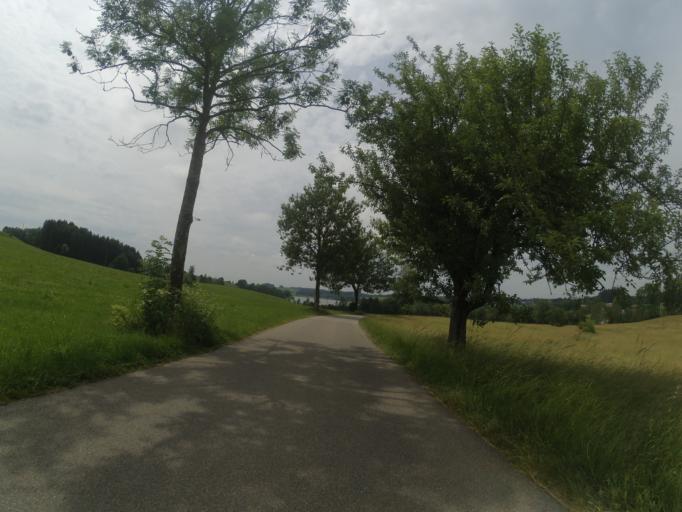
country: DE
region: Baden-Wuerttemberg
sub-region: Tuebingen Region
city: Isny im Allgau
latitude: 47.7508
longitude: 10.0138
